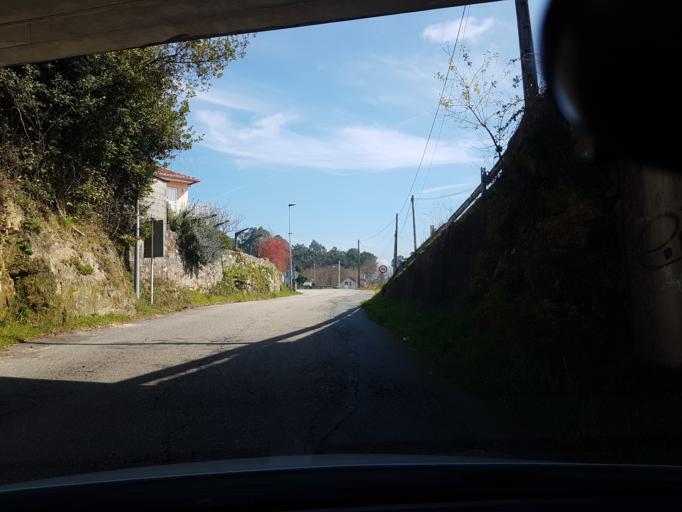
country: ES
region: Galicia
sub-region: Provincia de Pontevedra
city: Porrino
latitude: 42.2019
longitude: -8.6463
